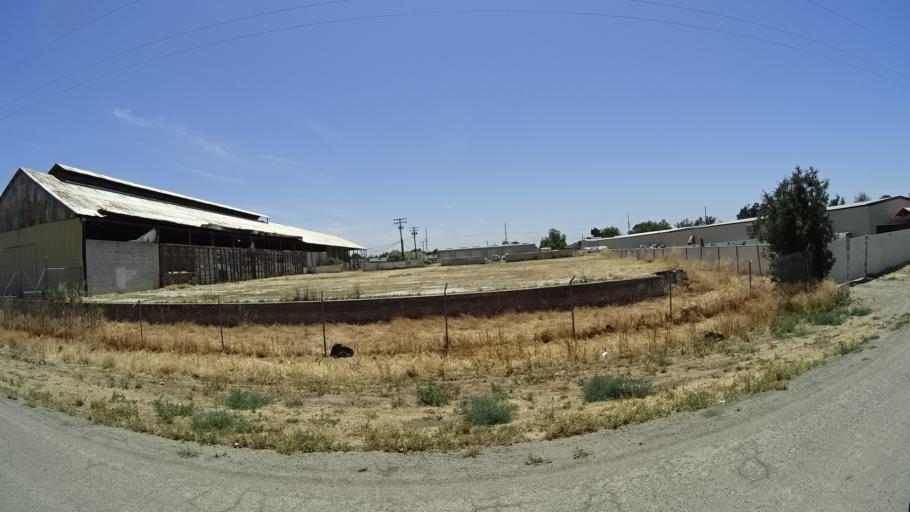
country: US
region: California
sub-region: Kings County
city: Armona
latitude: 36.3155
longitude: -119.7043
